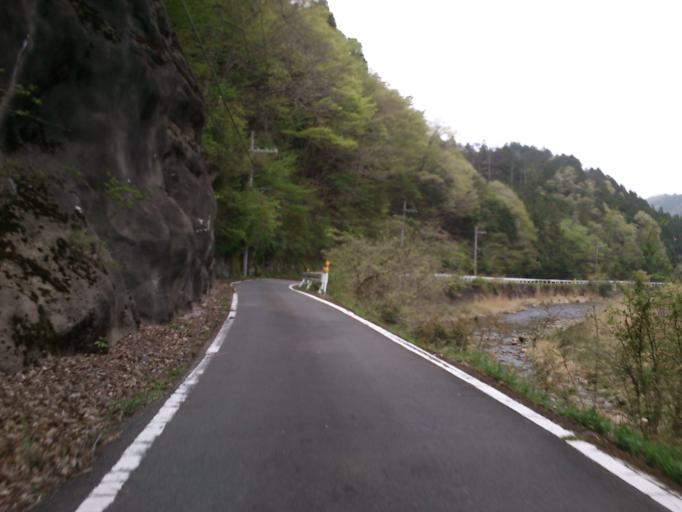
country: JP
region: Kyoto
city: Maizuru
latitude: 35.3960
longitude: 135.4735
